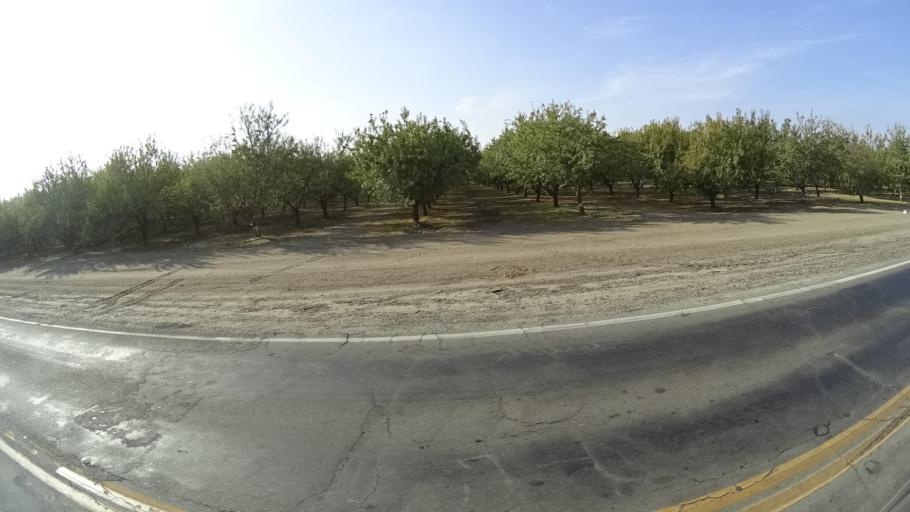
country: US
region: California
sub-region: Kern County
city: Delano
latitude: 35.7579
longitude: -119.2232
